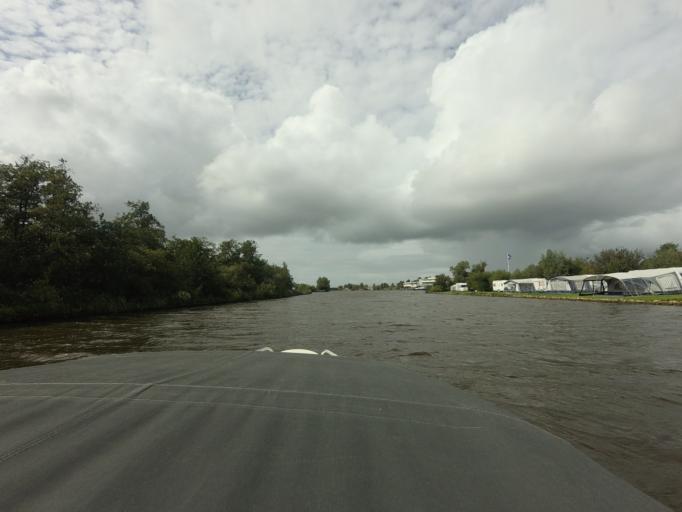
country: NL
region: Friesland
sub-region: Gemeente Boarnsterhim
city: Warten
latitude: 53.1262
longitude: 5.9368
